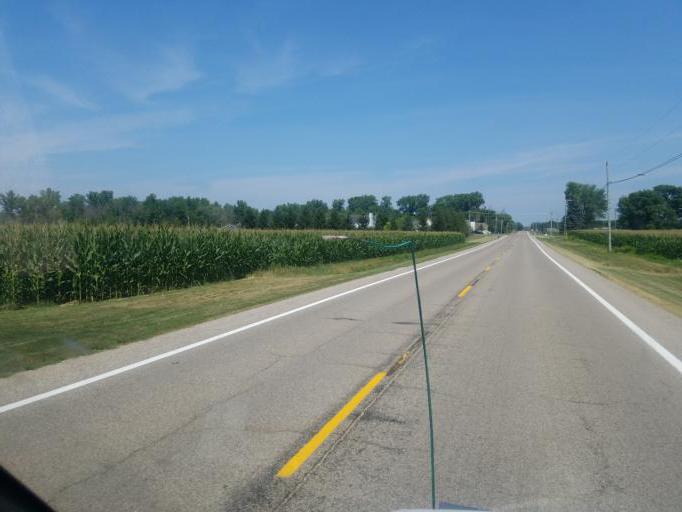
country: US
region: Ohio
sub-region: Mercer County
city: Celina
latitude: 40.5022
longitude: -84.5244
